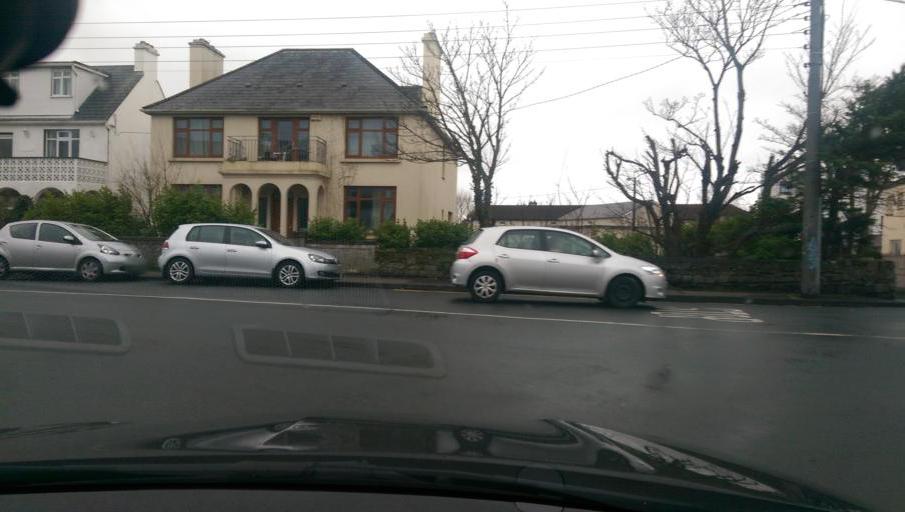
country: IE
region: Connaught
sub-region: County Galway
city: Gaillimh
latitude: 53.2675
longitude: -9.0671
